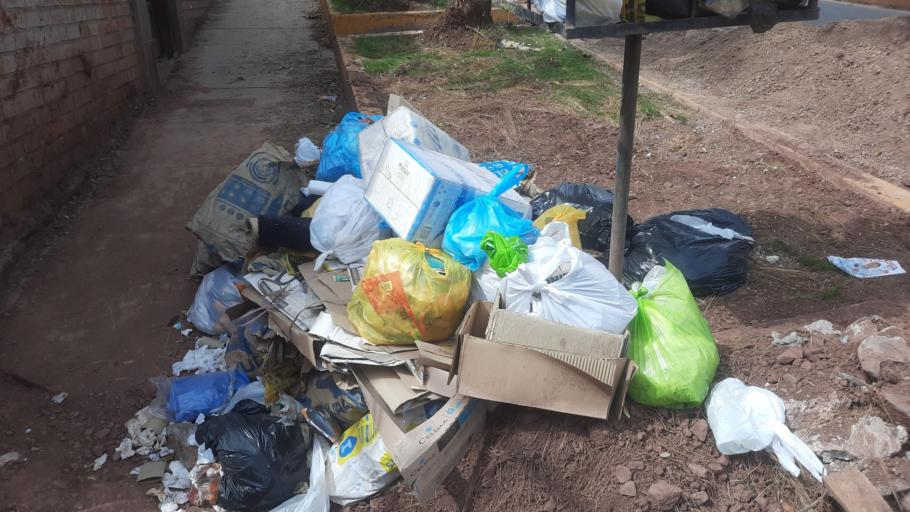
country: PE
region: Cusco
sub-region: Provincia de Cusco
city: Saylla
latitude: -13.5316
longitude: -71.9025
